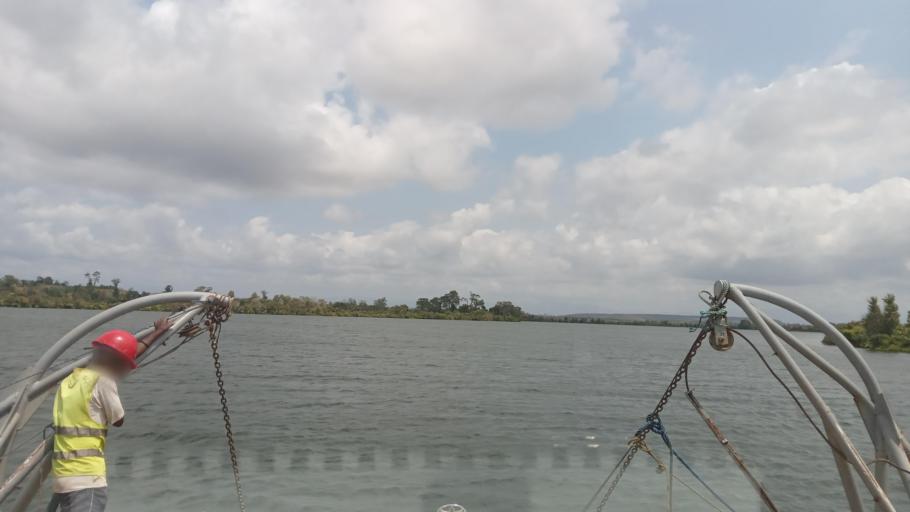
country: MG
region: Atsimo-Atsinanana
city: Vohipaho
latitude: -23.8136
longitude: 47.5486
